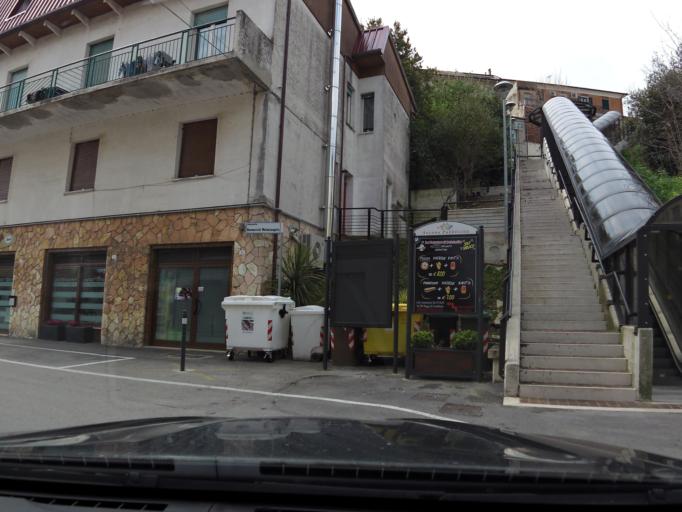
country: IT
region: The Marches
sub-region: Provincia di Ancona
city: Castelfidardo
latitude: 43.4639
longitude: 13.5503
